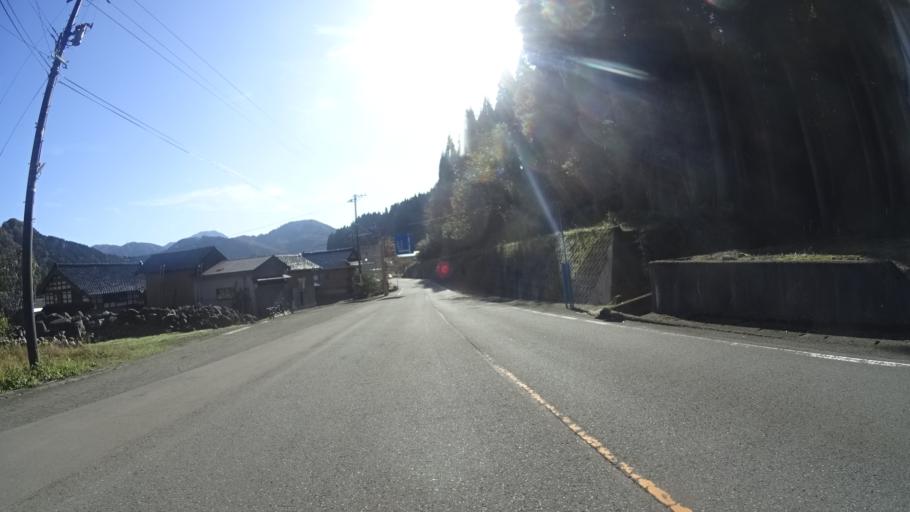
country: JP
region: Ishikawa
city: Tsurugi-asahimachi
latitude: 36.3652
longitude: 136.5914
